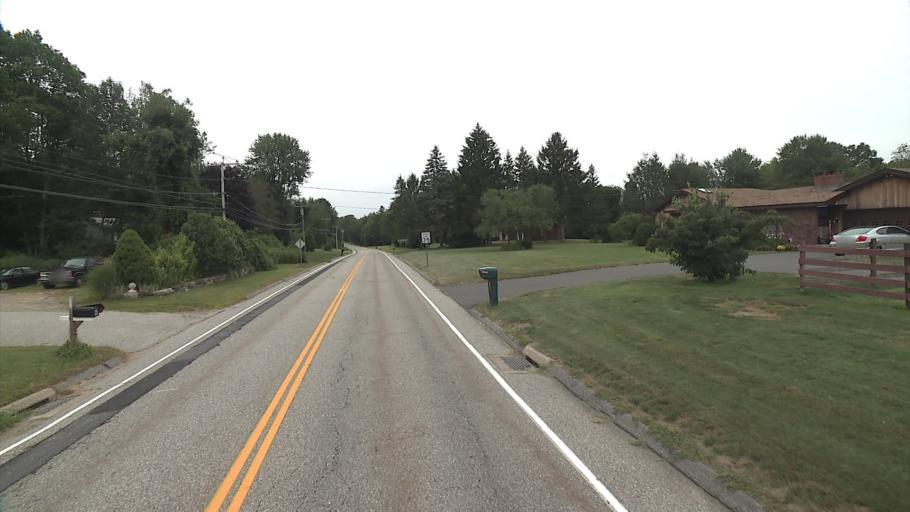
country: US
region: Connecticut
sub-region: Hartford County
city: Manchester
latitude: 41.7701
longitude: -72.4436
